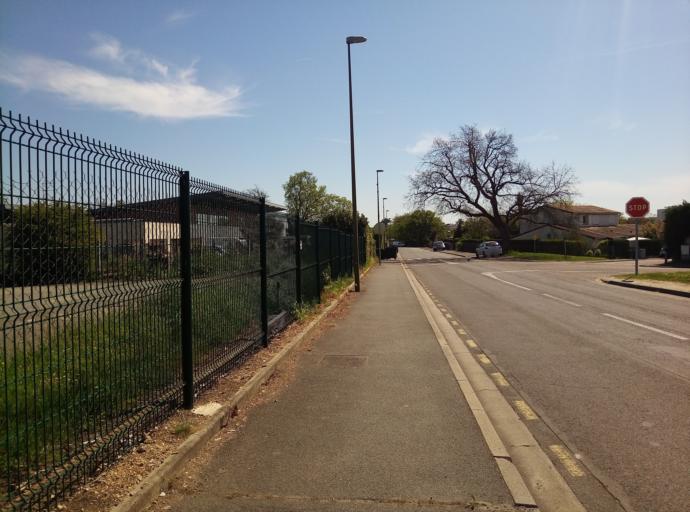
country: FR
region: Aquitaine
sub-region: Departement de la Gironde
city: Lormont
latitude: 44.8775
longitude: -0.5168
